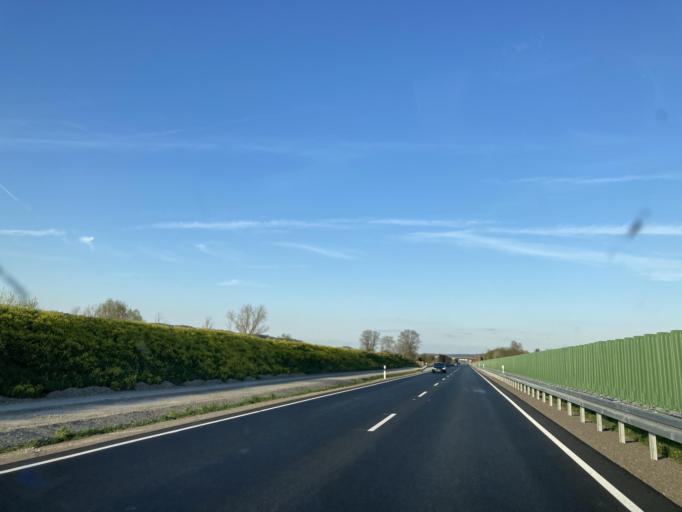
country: DE
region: Baden-Wuerttemberg
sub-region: Tuebingen Region
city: Rottenburg
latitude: 48.4844
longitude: 8.9899
